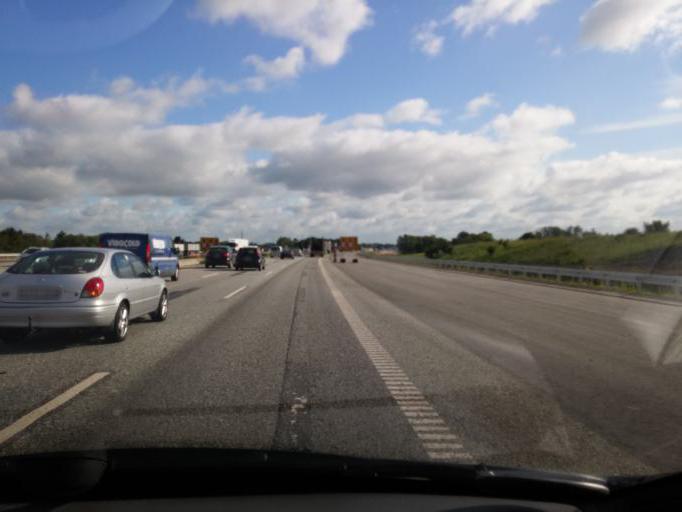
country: DK
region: Zealand
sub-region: Solrod Kommune
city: Solrod
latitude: 55.5068
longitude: 12.1773
